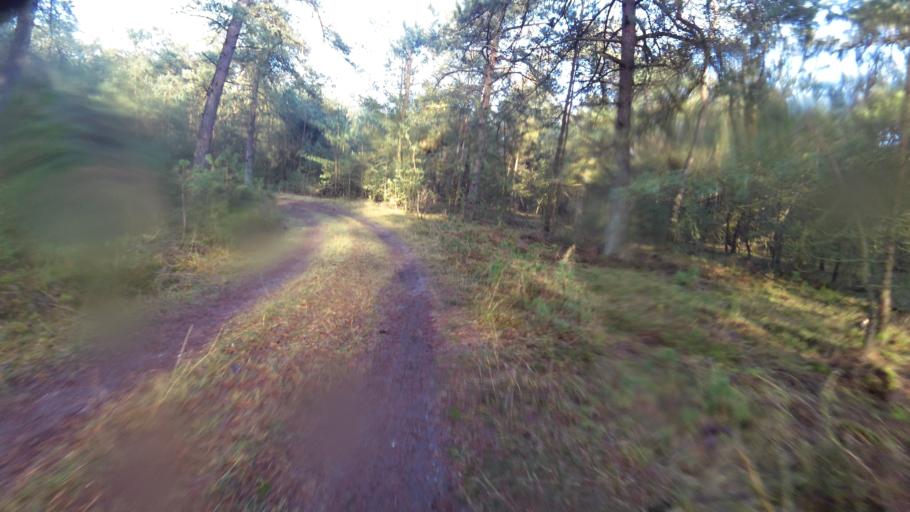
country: NL
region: Gelderland
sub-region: Gemeente Barneveld
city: Garderen
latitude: 52.2027
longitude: 5.7392
